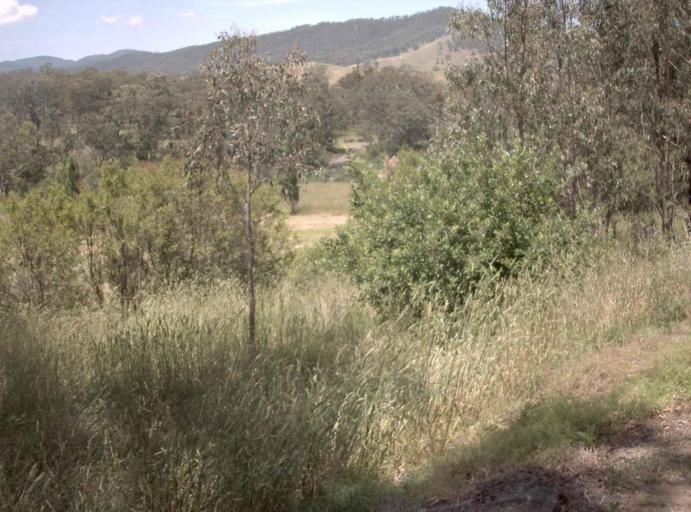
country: AU
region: Victoria
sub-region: East Gippsland
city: Bairnsdale
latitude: -37.4071
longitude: 147.8363
